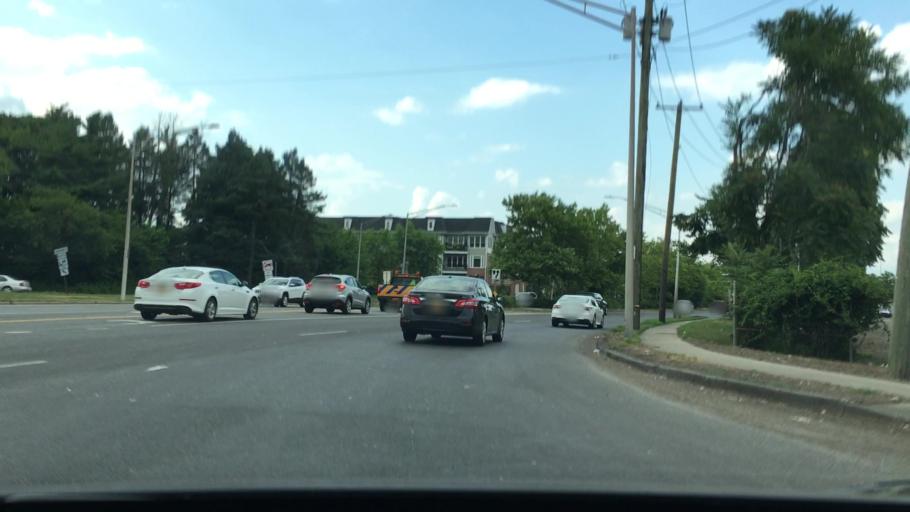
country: US
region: New York
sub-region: Nassau County
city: East Garden City
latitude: 40.7383
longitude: -73.5934
